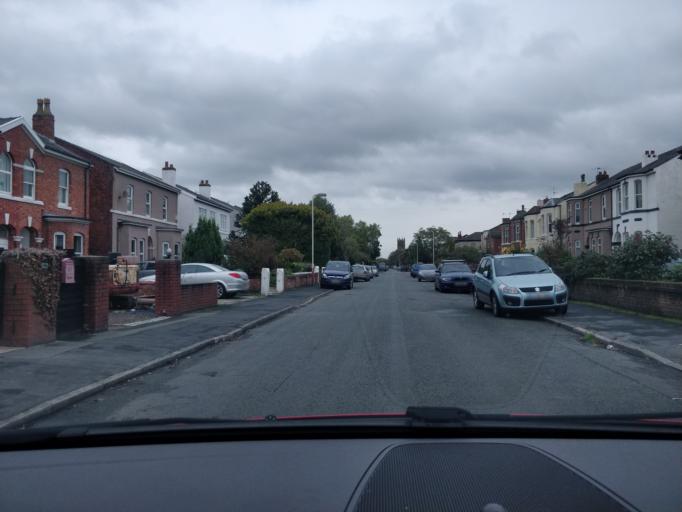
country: GB
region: England
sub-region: Sefton
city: Southport
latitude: 53.6373
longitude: -2.9998
